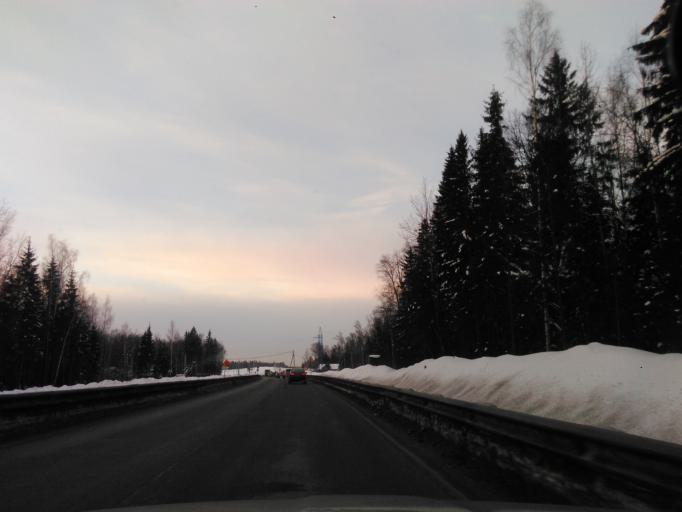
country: RU
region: Moskovskaya
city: Povarovo
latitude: 56.0140
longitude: 37.0284
